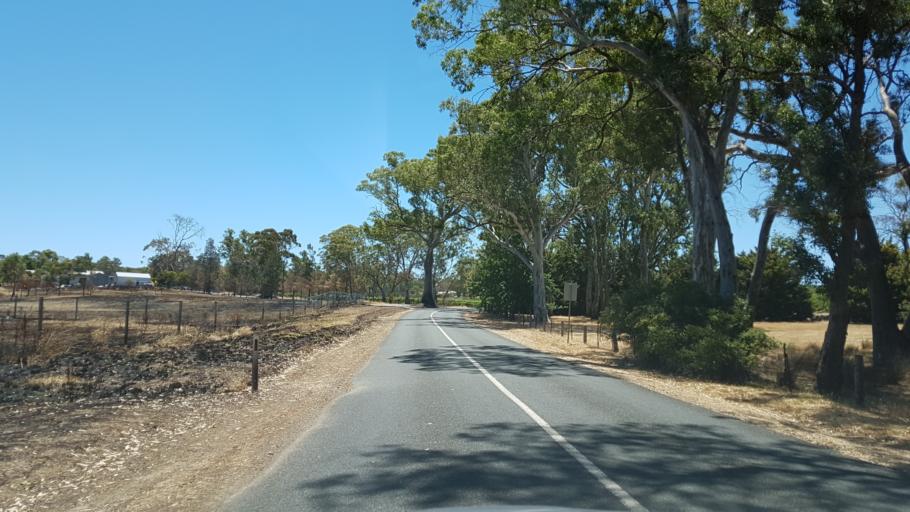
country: AU
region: South Australia
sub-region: Adelaide Hills
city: Lobethal
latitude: -34.8945
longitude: 138.9044
